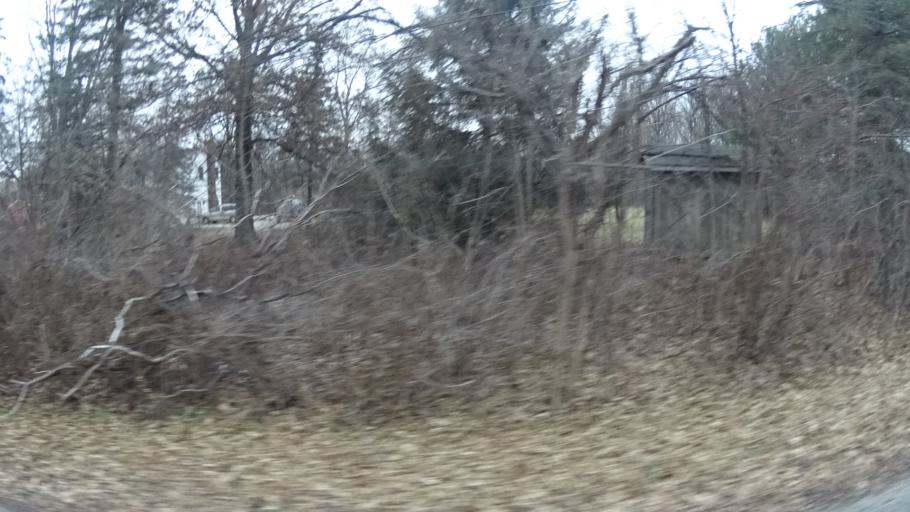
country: US
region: Ohio
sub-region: Lorain County
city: Grafton
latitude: 41.2563
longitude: -82.0264
